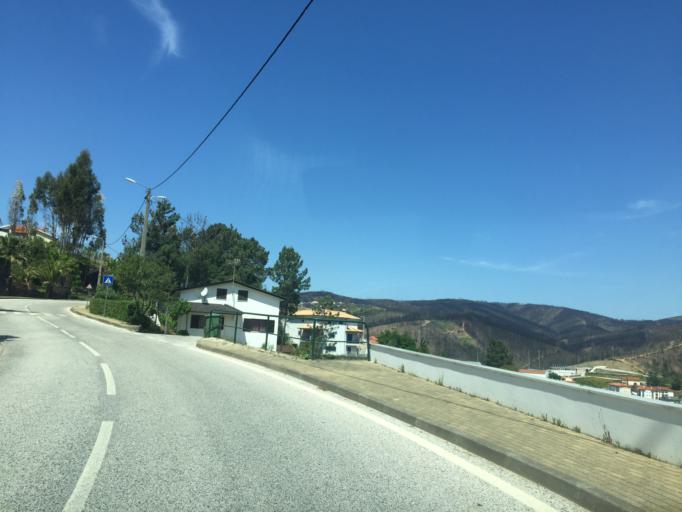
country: PT
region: Coimbra
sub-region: Pampilhosa da Serra
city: Pampilhosa da Serra
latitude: 40.0444
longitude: -7.9523
